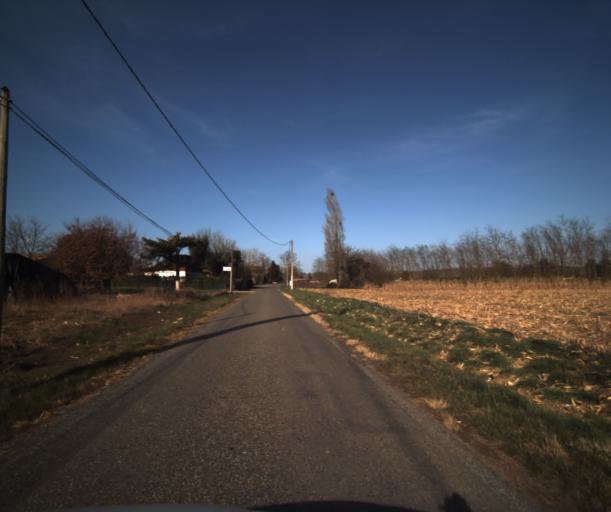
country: FR
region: Midi-Pyrenees
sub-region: Departement du Tarn-et-Garonne
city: Labastide-Saint-Pierre
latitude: 43.9269
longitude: 1.3543
